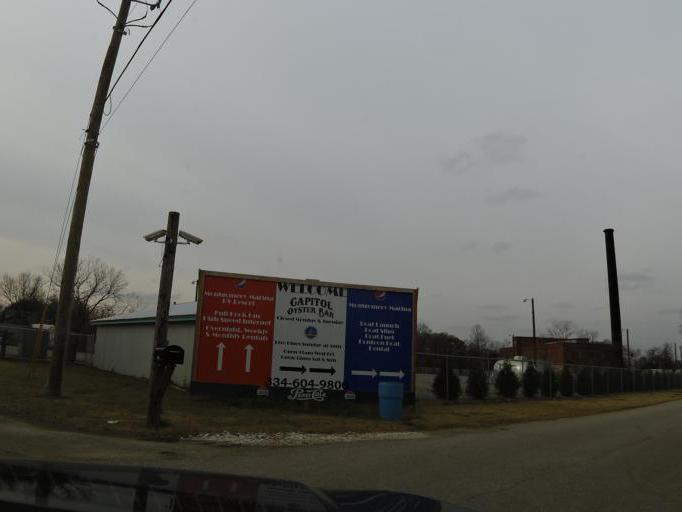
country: US
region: Alabama
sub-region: Montgomery County
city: Montgomery
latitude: 32.3936
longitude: -86.3145
